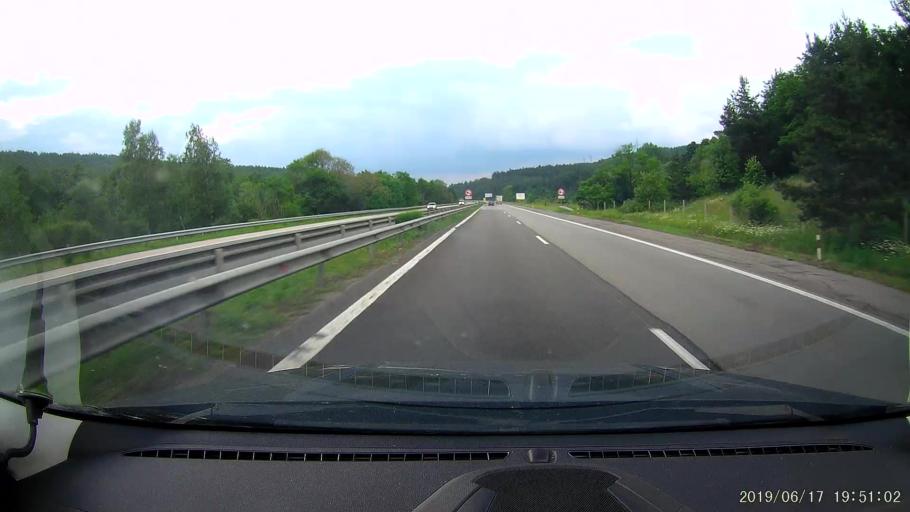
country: BG
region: Sofiya
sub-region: Obshtina Ikhtiman
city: Ikhtiman
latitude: 42.5034
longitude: 23.7685
